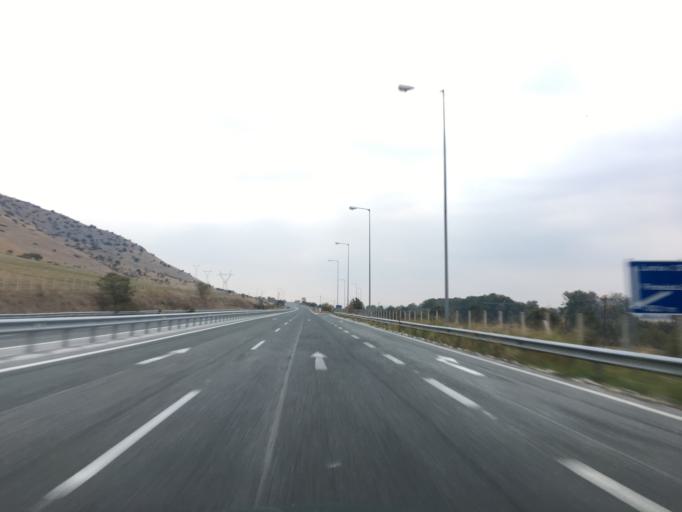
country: GR
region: Thessaly
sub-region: Trikala
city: Zarkos
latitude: 39.5881
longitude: 22.1553
